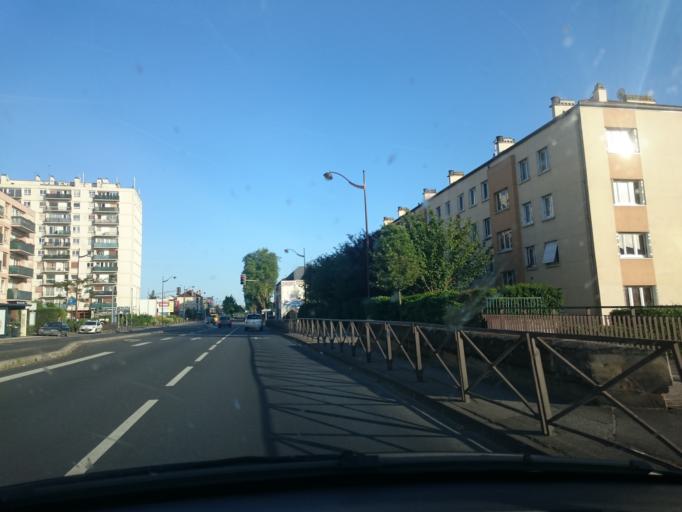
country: FR
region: Ile-de-France
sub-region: Departement de l'Essonne
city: Juvisy-sur-Orge
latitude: 48.6764
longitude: 2.3847
